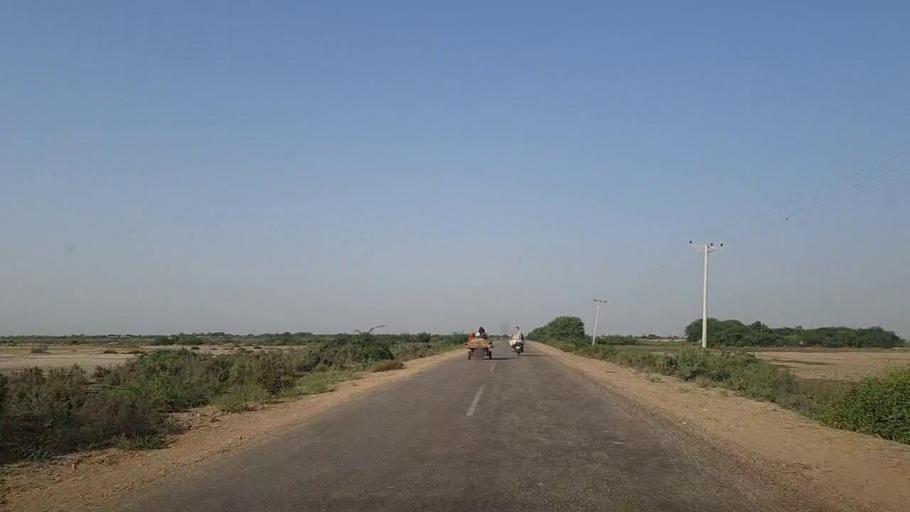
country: PK
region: Sindh
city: Mirpur Batoro
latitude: 24.6088
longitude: 68.4029
